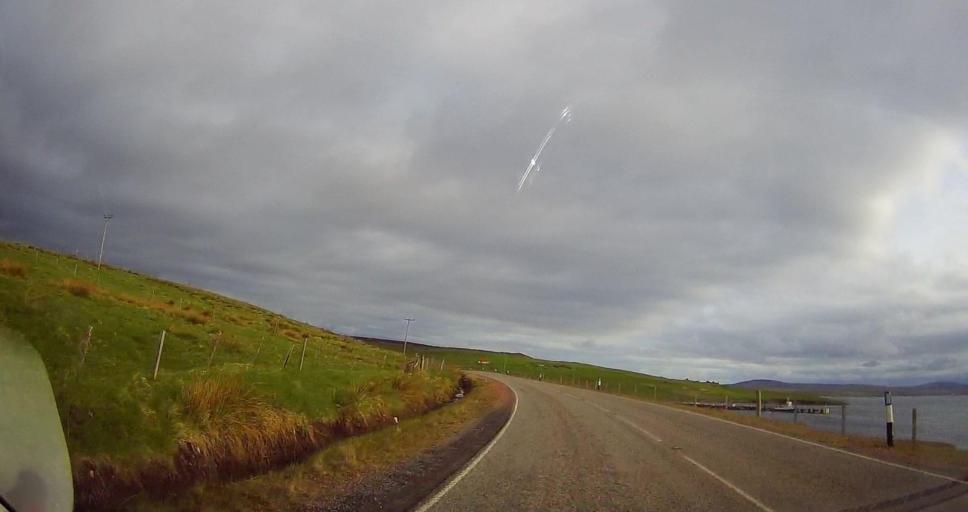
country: GB
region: Scotland
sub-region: Shetland Islands
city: Lerwick
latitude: 60.4607
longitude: -1.2091
